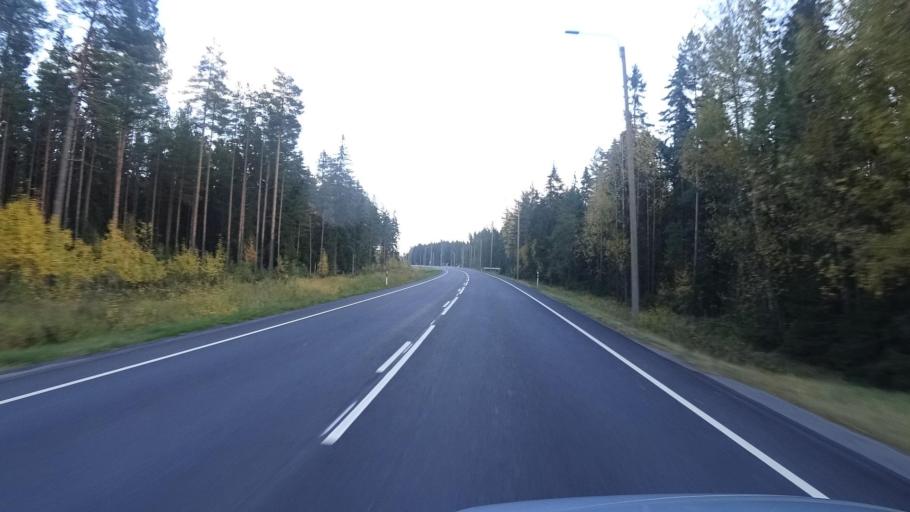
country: FI
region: Satakunta
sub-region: Rauma
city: Koeylioe
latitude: 61.0919
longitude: 22.2435
